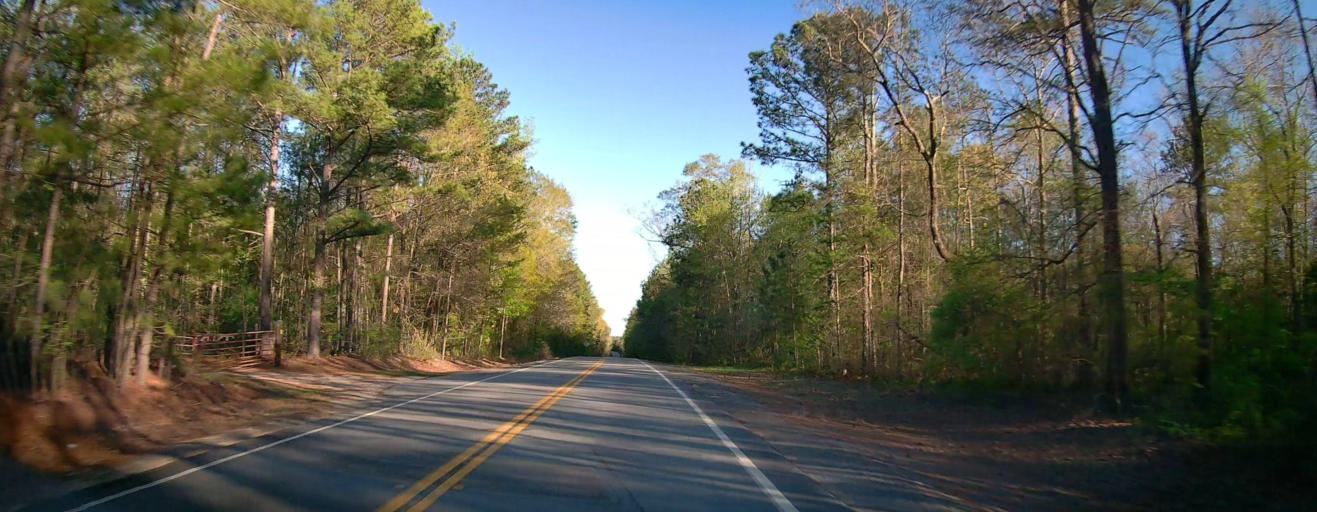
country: US
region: Georgia
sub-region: Wilkinson County
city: Irwinton
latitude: 32.9364
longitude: -83.1498
